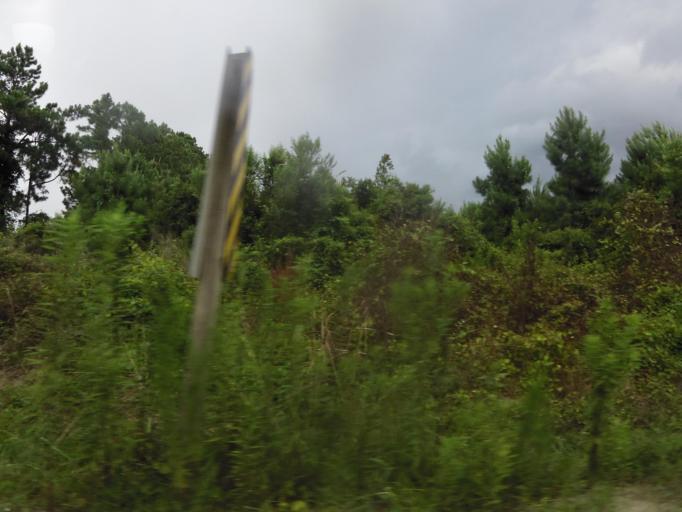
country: US
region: Georgia
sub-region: Camden County
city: Kingsland
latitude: 30.7825
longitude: -81.6424
